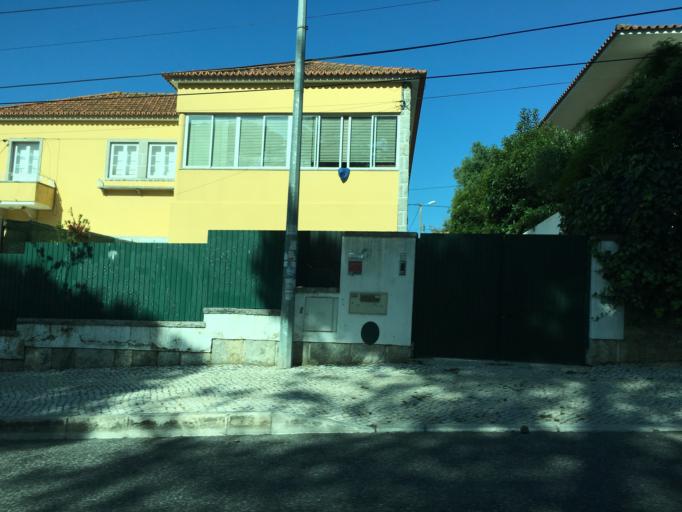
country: PT
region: Lisbon
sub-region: Cascais
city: Monte Estoril
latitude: 38.7090
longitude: -9.4179
